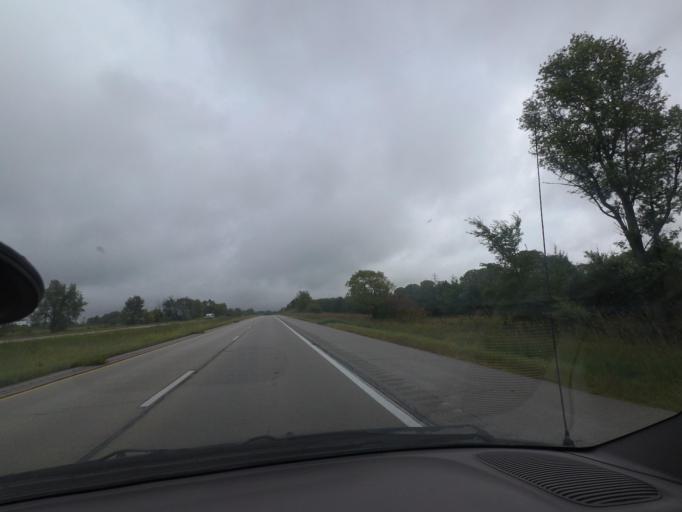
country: US
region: Illinois
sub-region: Piatt County
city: Monticello
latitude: 40.0640
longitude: -88.5506
